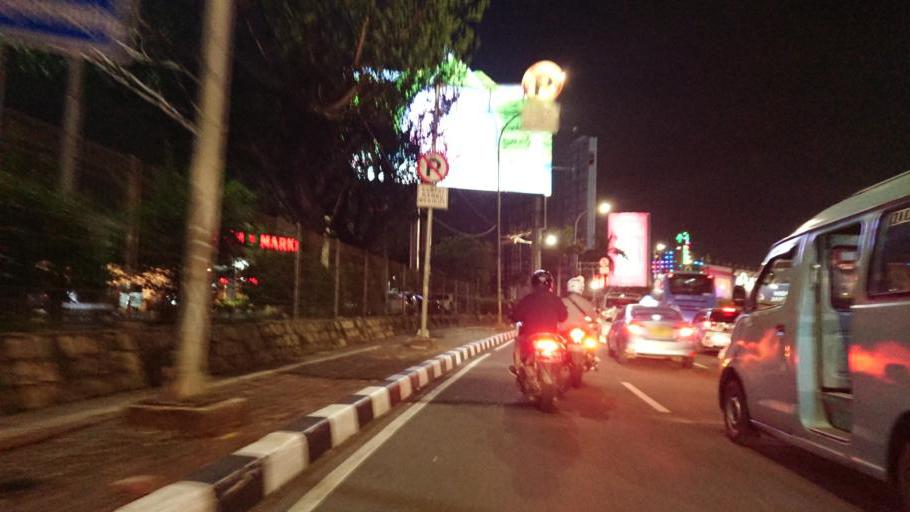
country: ID
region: Banten
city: South Tangerang
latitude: -6.2625
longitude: 106.7832
